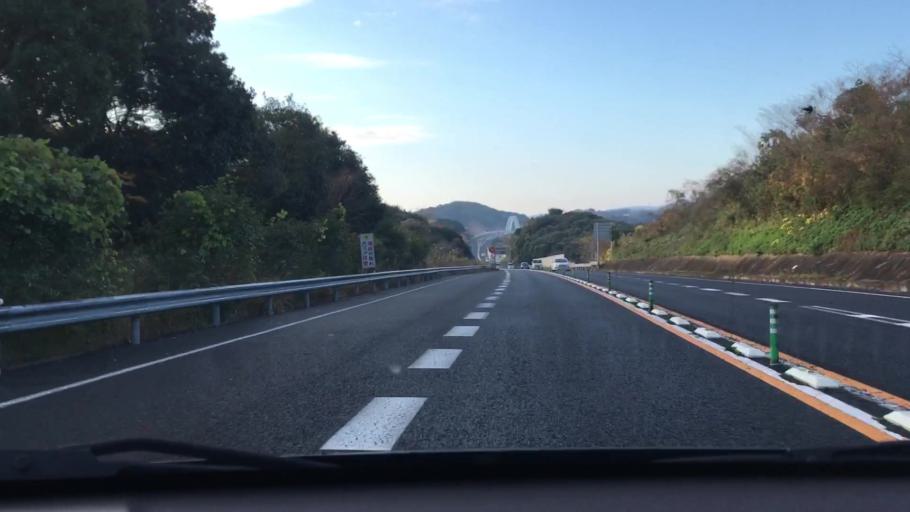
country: JP
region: Nagasaki
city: Sasebo
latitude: 33.0635
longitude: 129.7606
